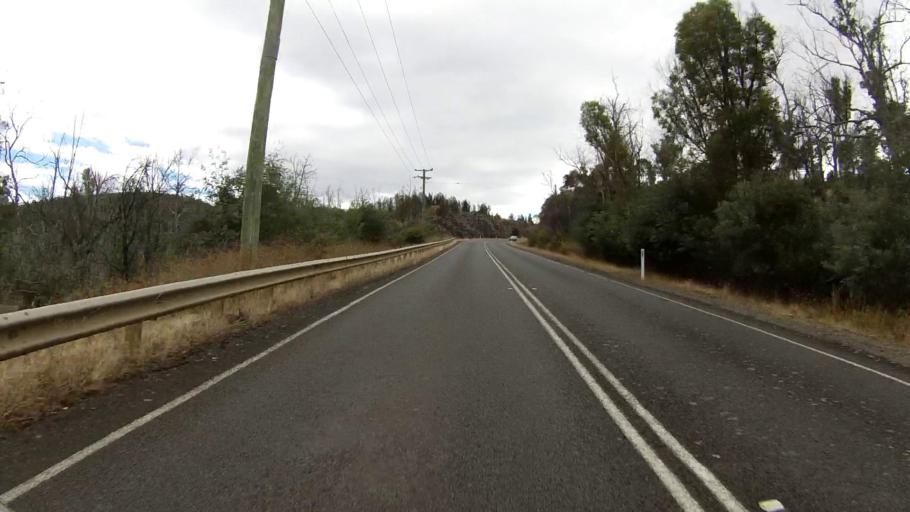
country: AU
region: Tasmania
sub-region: Sorell
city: Sorell
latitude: -42.5888
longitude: 147.7989
